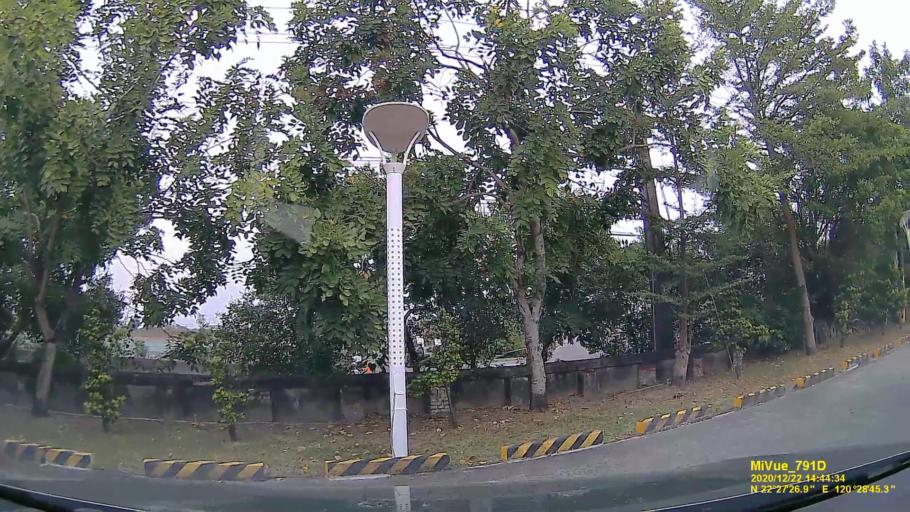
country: TW
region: Taiwan
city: Fengshan
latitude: 22.4575
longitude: 120.4792
